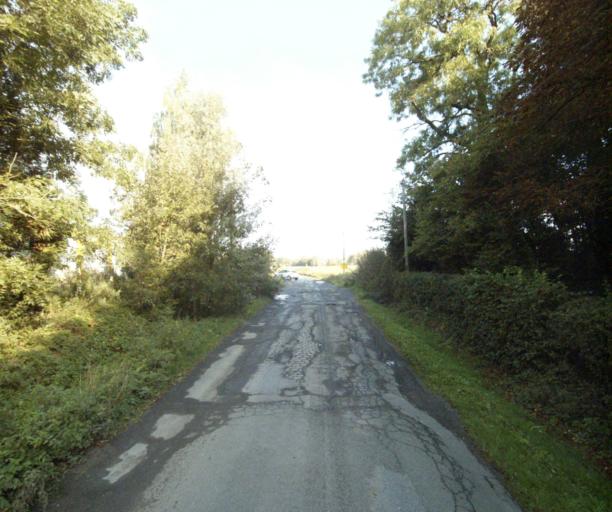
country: FR
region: Nord-Pas-de-Calais
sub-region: Departement du Nord
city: Lomme
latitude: 50.6548
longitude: 2.9935
